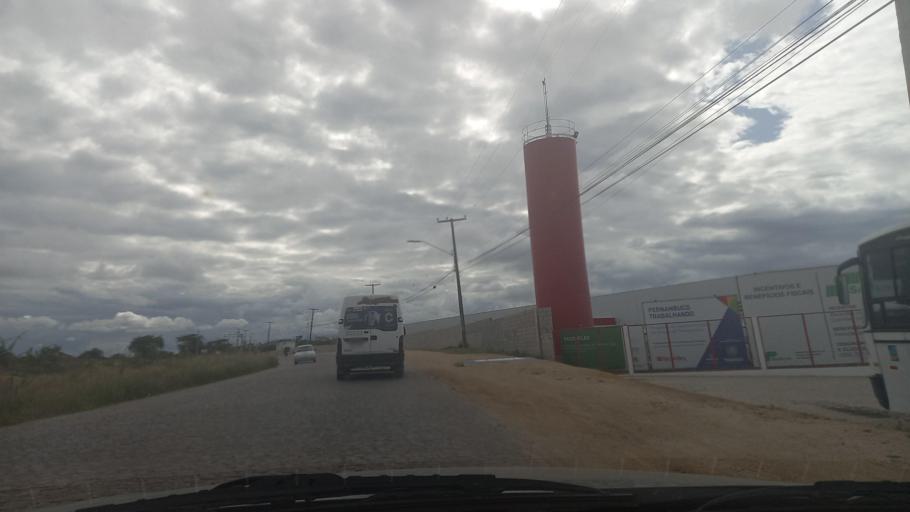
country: BR
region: Pernambuco
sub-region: Caruaru
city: Caruaru
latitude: -8.2898
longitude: -36.0197
